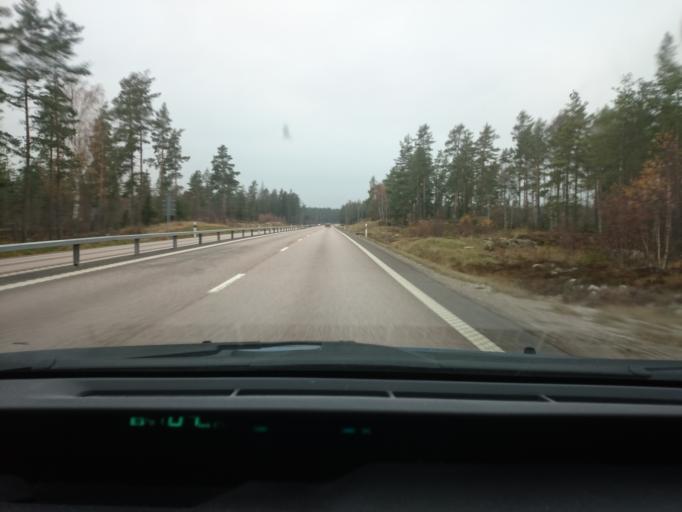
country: SE
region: Vaestmanland
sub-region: Sala Kommun
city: Sala
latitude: 60.0022
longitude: 16.4152
